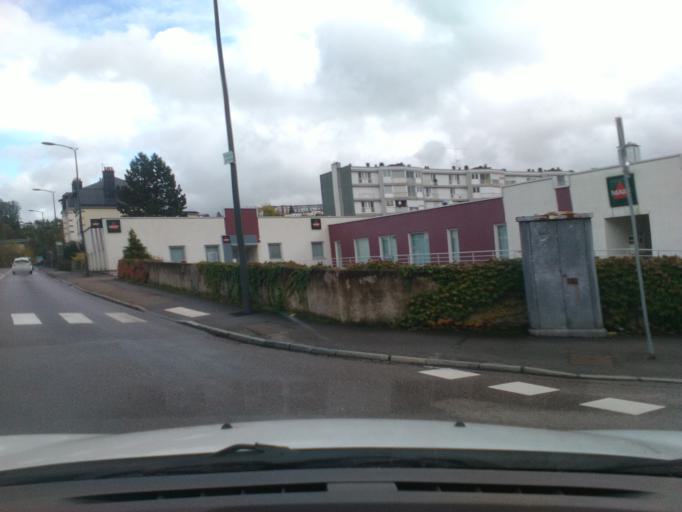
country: FR
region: Lorraine
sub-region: Departement des Vosges
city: Epinal
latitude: 48.1832
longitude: 6.4423
